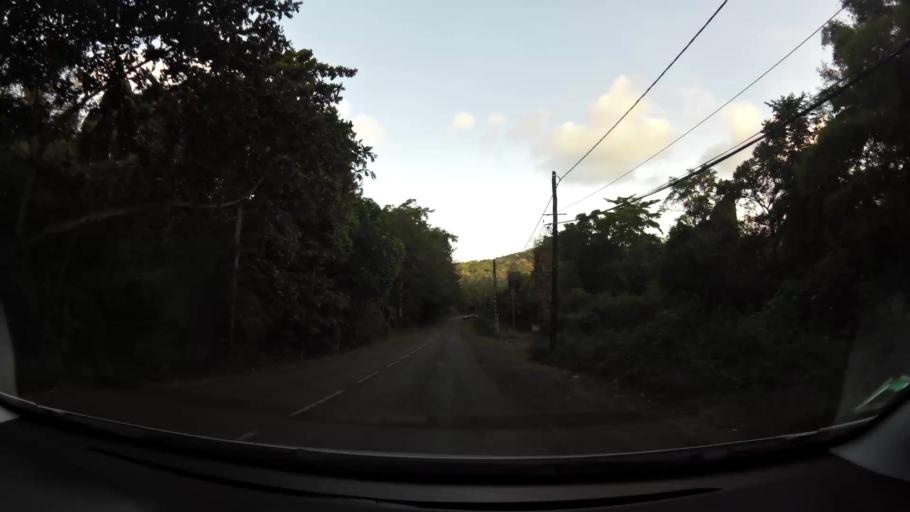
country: YT
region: Dembeni
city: Dembeni
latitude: -12.8621
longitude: 45.1977
